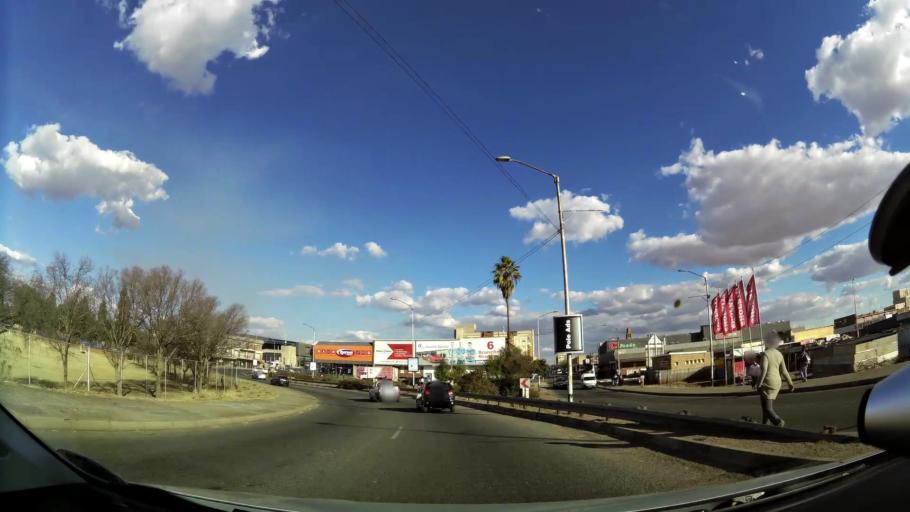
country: ZA
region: North-West
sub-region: Dr Kenneth Kaunda District Municipality
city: Klerksdorp
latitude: -26.8625
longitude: 26.6656
